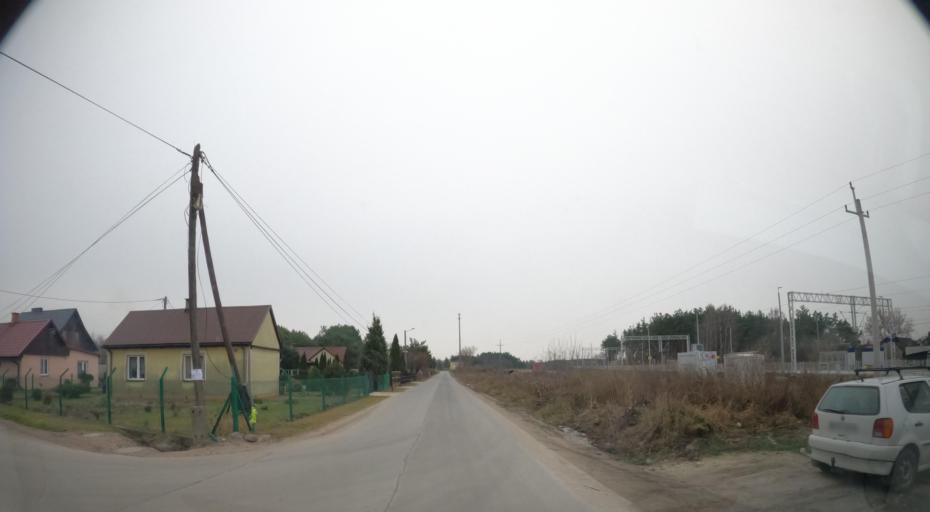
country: PL
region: Masovian Voivodeship
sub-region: Powiat radomski
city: Jastrzebia
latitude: 51.4802
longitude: 21.1942
